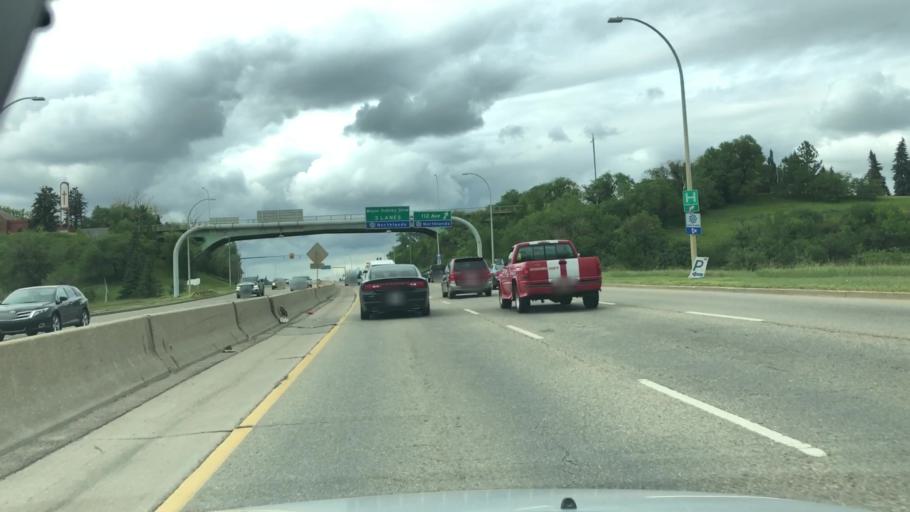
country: CA
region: Alberta
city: Edmonton
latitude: 53.5589
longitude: -113.4411
